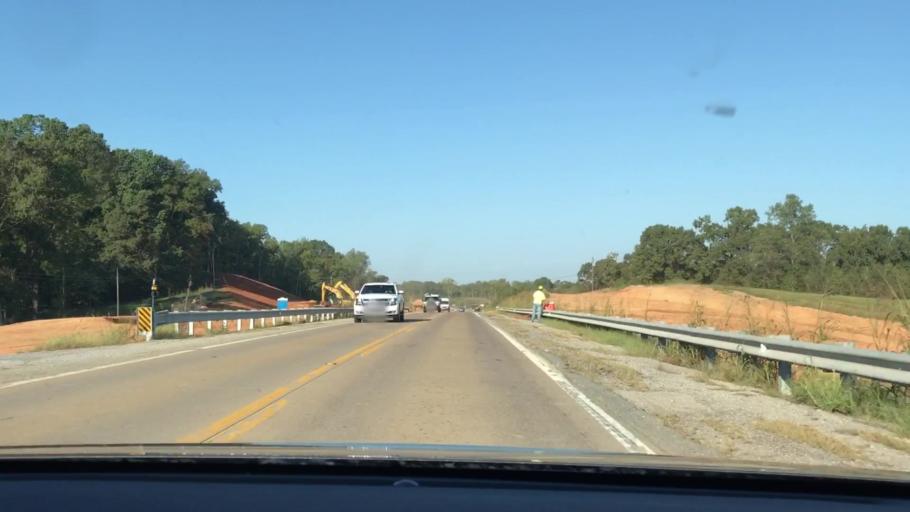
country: US
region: Kentucky
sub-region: Trigg County
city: Cadiz
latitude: 36.7985
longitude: -87.9507
